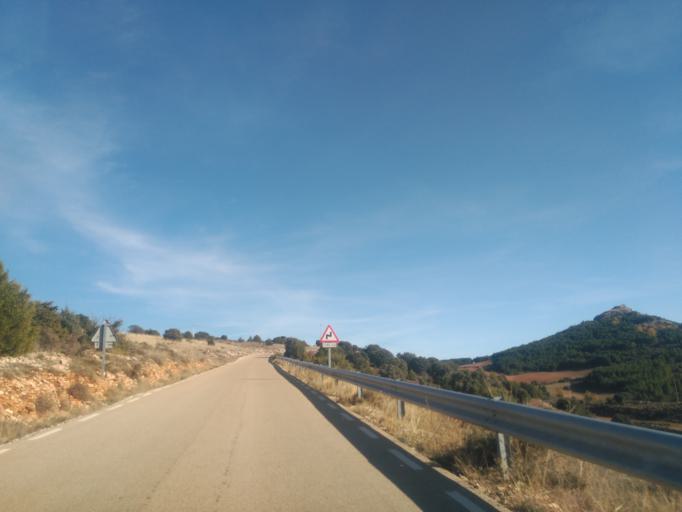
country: ES
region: Castille and Leon
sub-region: Provincia de Soria
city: Espejon
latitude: 41.8324
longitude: -3.2523
